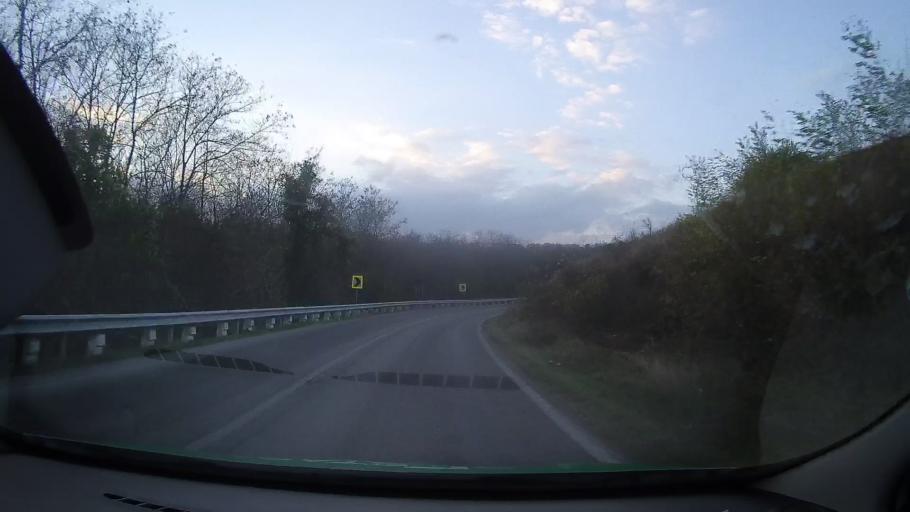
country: RO
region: Constanta
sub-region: Comuna Baneasa
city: Baneasa
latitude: 44.0764
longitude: 27.6696
